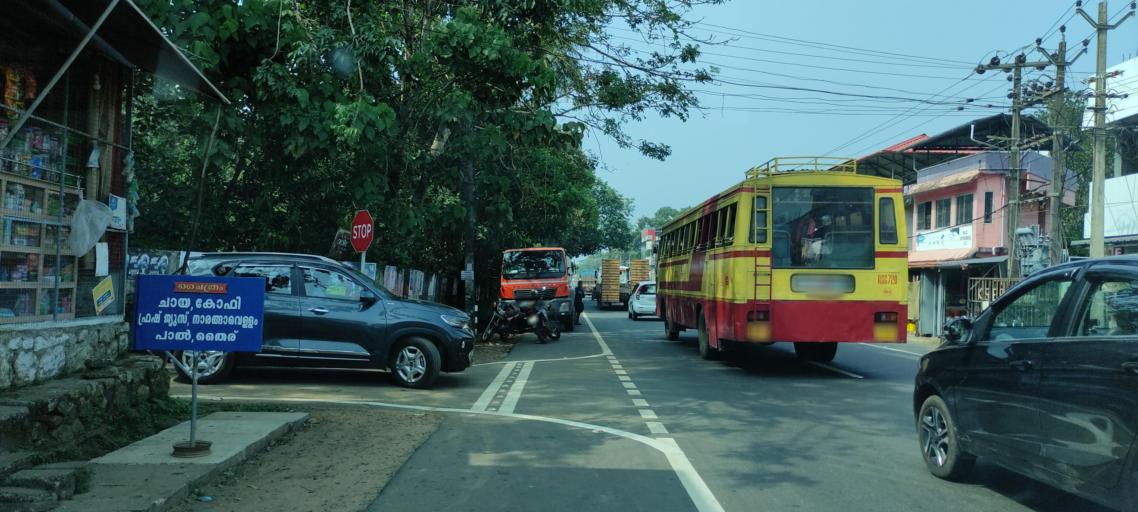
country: IN
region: Kerala
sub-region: Pattanamtitta
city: Adur
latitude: 9.2122
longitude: 76.6846
